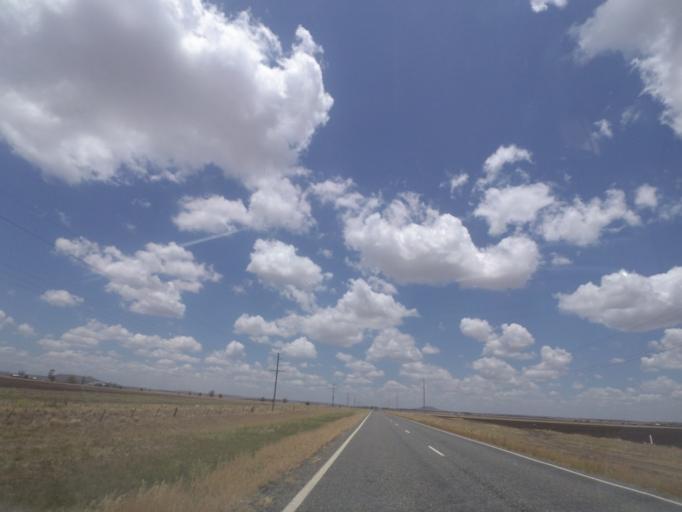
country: AU
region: Queensland
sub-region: Toowoomba
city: Top Camp
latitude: -27.9001
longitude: 151.9760
